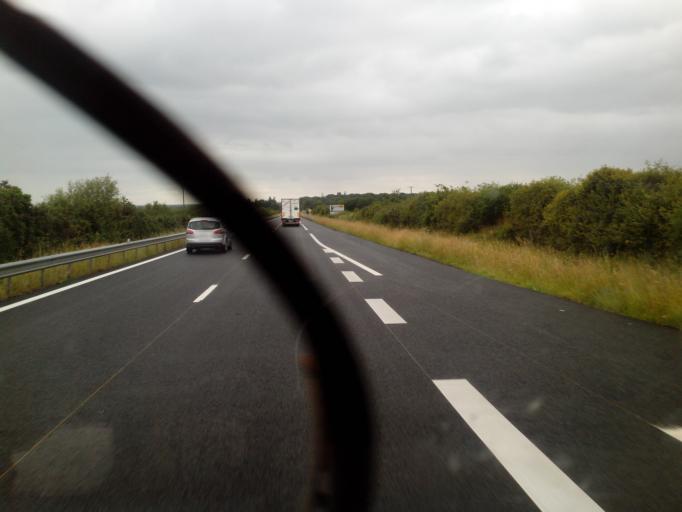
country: FR
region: Pays de la Loire
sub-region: Departement de la Loire-Atlantique
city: La Grigonnais
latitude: 47.5122
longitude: -1.6396
